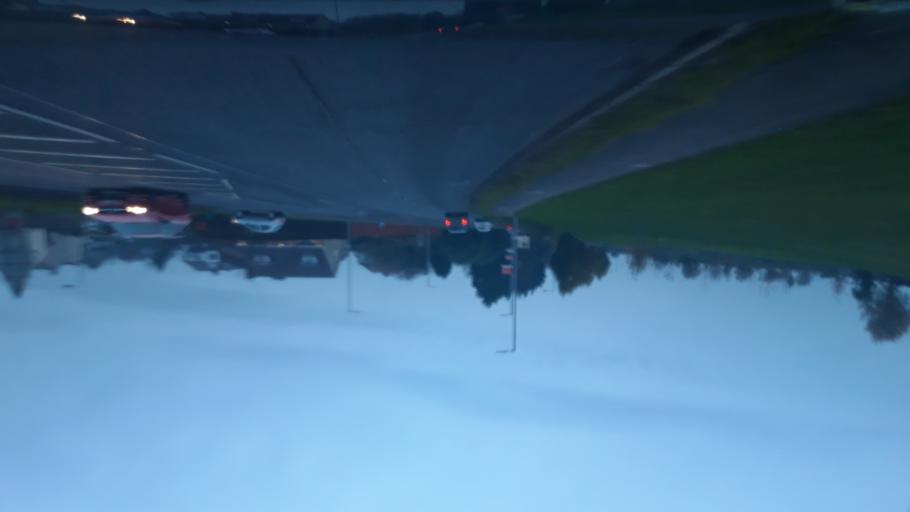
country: GB
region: Northern Ireland
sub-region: Newry and Mourne District
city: Newry
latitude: 54.1845
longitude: -6.3566
